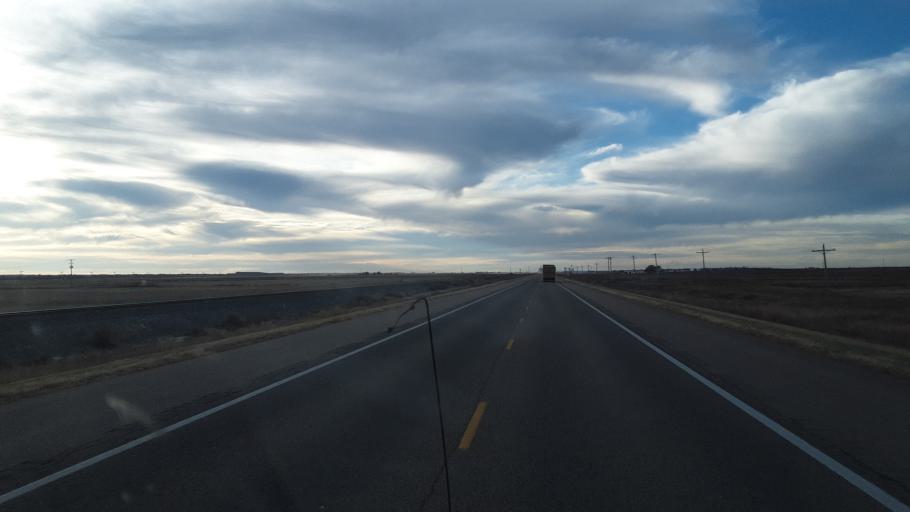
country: US
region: Kansas
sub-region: Hamilton County
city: Syracuse
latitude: 37.9665
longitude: -101.6935
